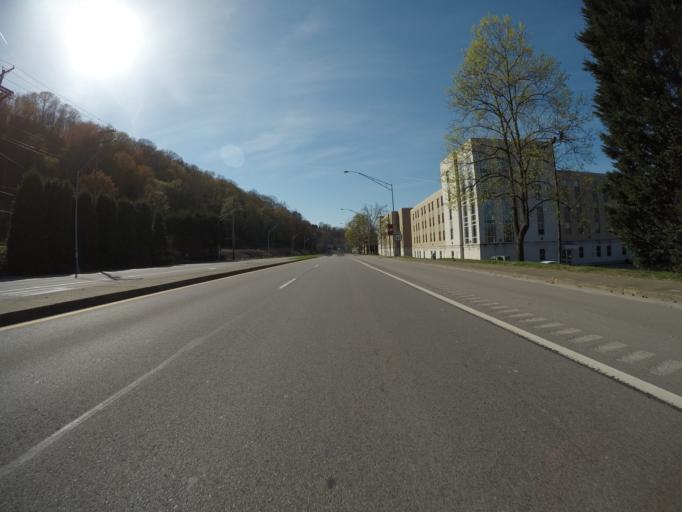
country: US
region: West Virginia
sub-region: Kanawha County
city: Charleston
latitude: 38.3318
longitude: -81.6163
